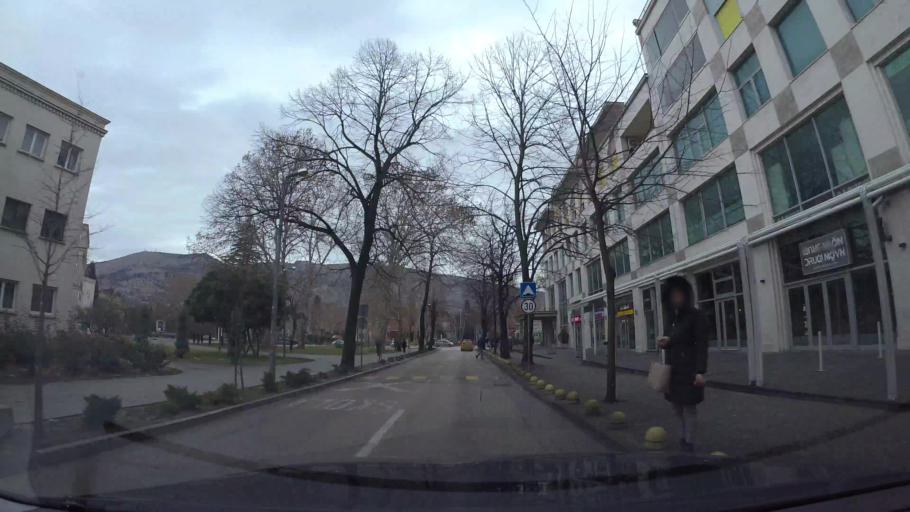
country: BA
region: Federation of Bosnia and Herzegovina
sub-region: Hercegovacko-Bosanski Kanton
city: Mostar
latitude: 43.3419
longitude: 17.8018
